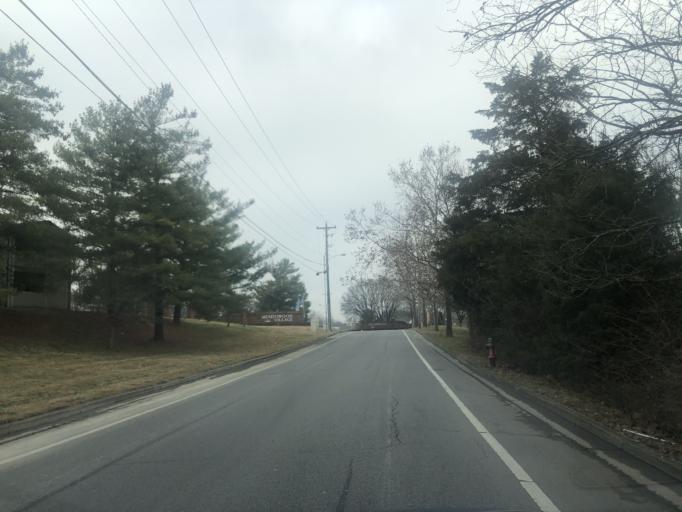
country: US
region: Tennessee
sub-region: Rutherford County
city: La Vergne
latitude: 36.0696
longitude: -86.6409
